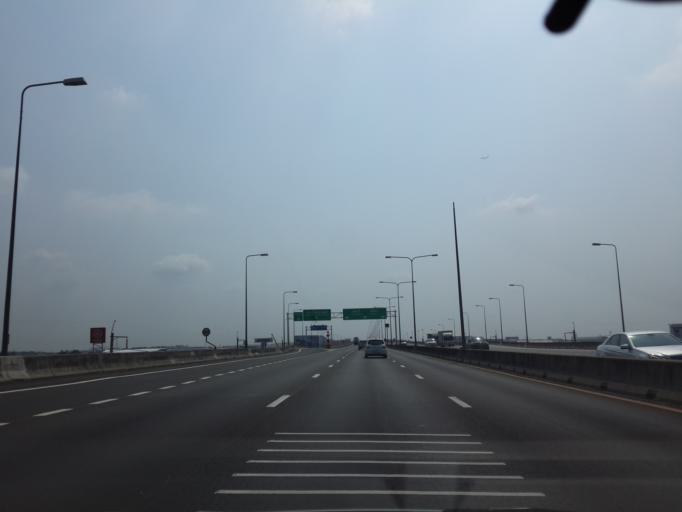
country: TH
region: Samut Prakan
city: Bang Bo District
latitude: 13.6098
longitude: 100.7631
